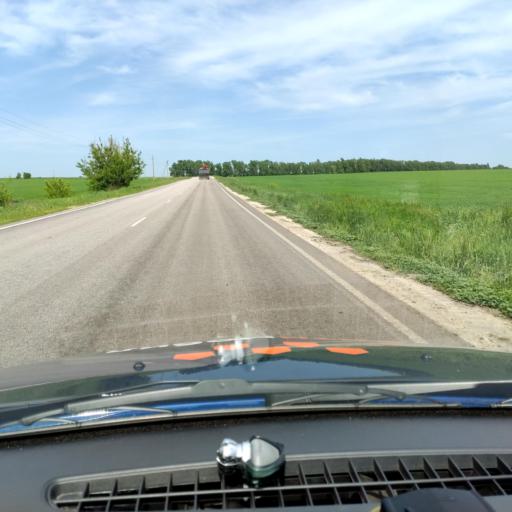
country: RU
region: Voronezj
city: Novaya Usman'
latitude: 51.5530
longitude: 39.3719
